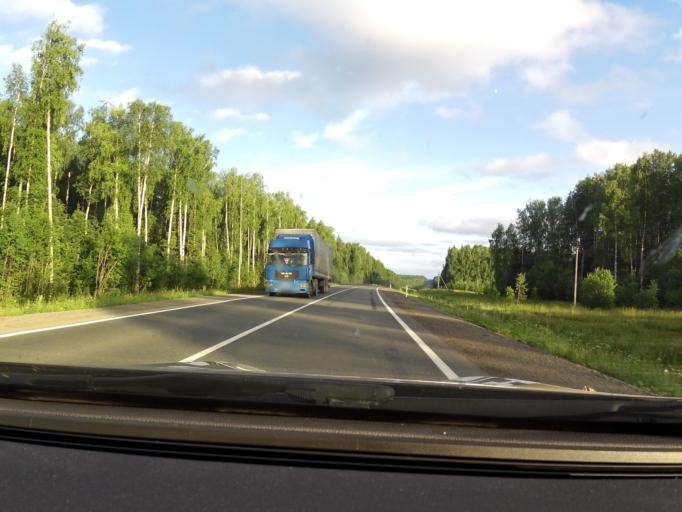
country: RU
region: Perm
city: Siva
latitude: 58.5959
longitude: 53.8782
